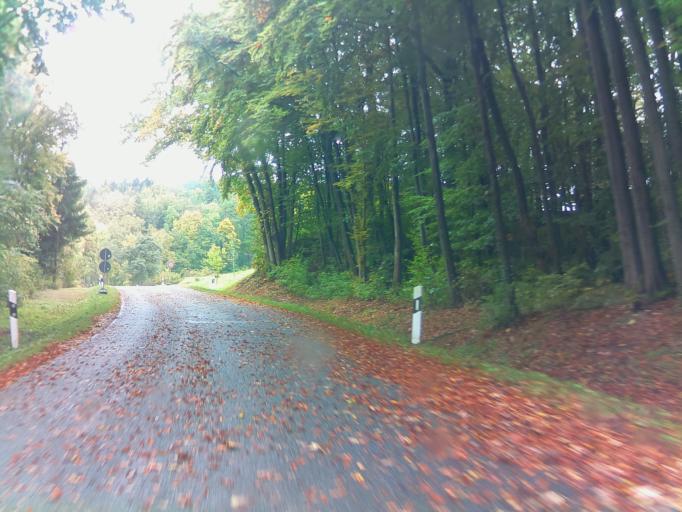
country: DE
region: Bavaria
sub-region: Upper Franconia
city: Altendorf
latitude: 50.0879
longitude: 11.1322
